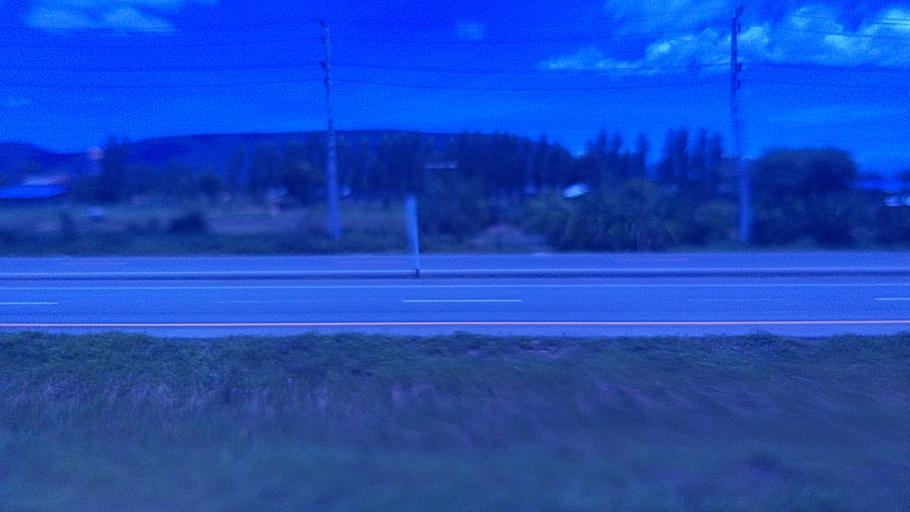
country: TH
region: Chaiyaphum
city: Phu Khiao
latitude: 16.2855
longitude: 102.2091
